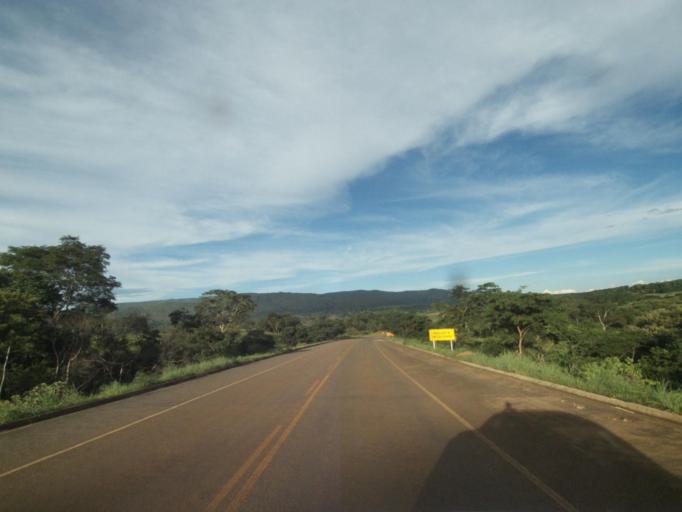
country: BR
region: Goias
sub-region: Jaragua
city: Jaragua
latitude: -15.8443
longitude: -49.3644
